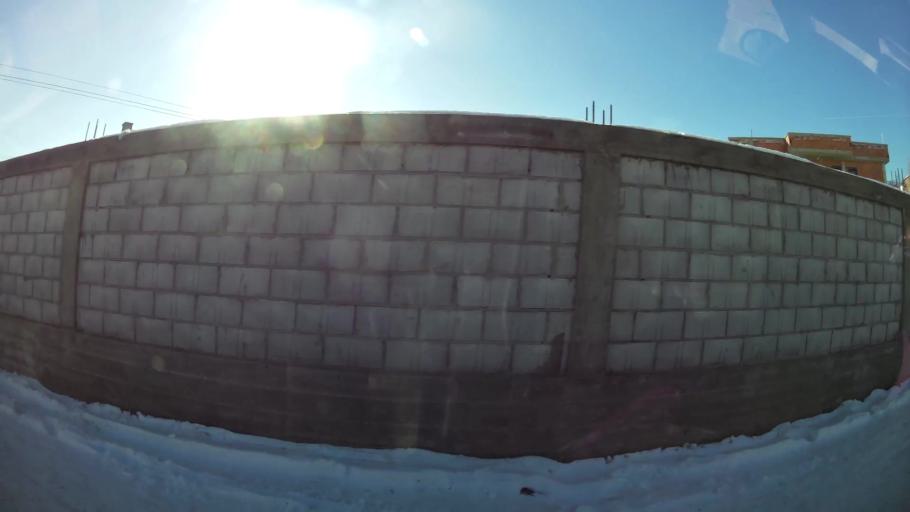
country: MK
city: Ljubin
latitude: 42.0026
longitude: 21.3120
